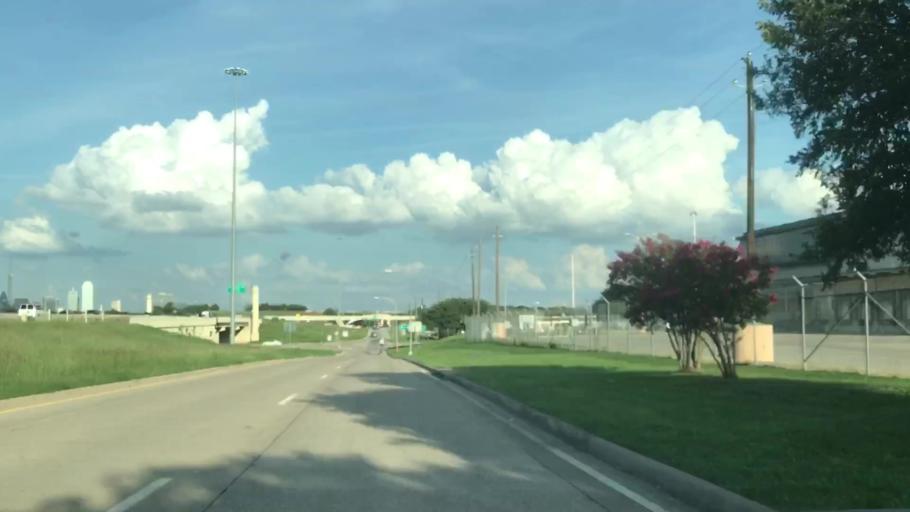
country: US
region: Texas
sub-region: Dallas County
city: Cockrell Hill
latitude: 32.7667
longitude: -96.8647
